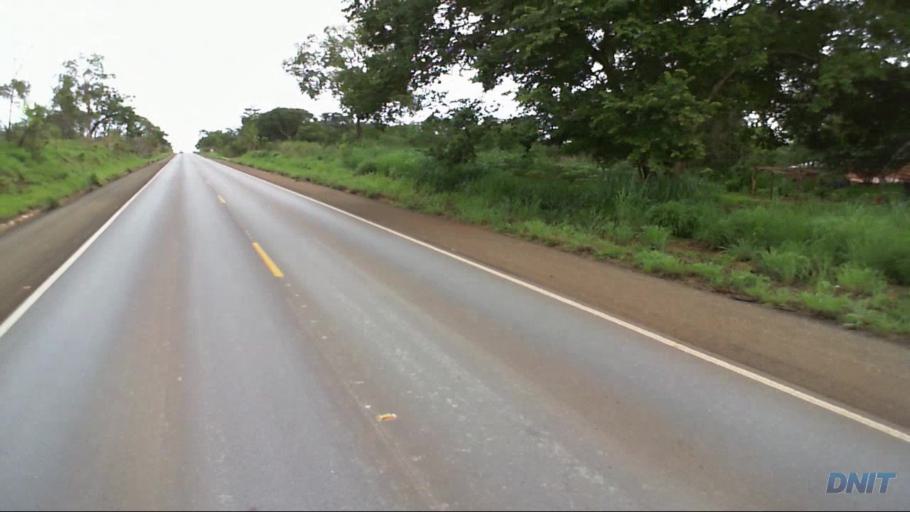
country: BR
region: Goias
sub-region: Barro Alto
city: Barro Alto
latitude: -14.8064
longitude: -49.0460
